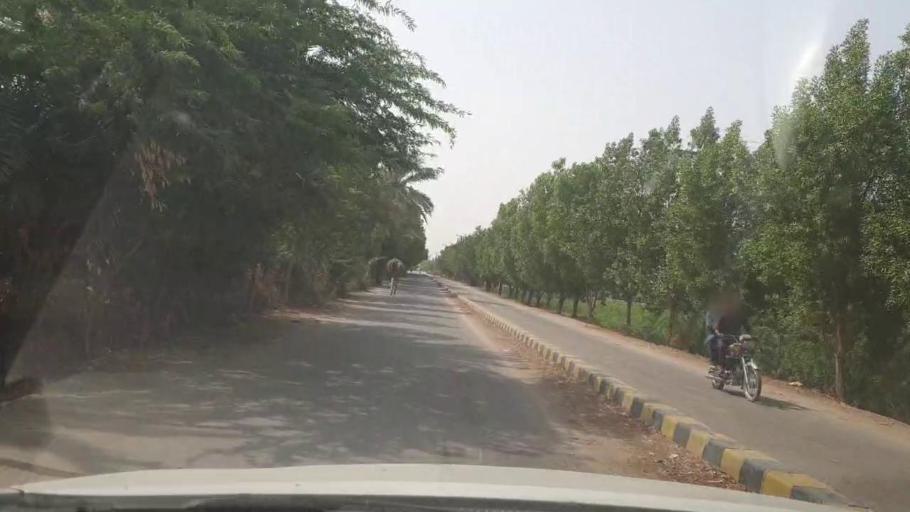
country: PK
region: Sindh
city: Kot Diji
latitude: 27.3524
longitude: 68.7116
